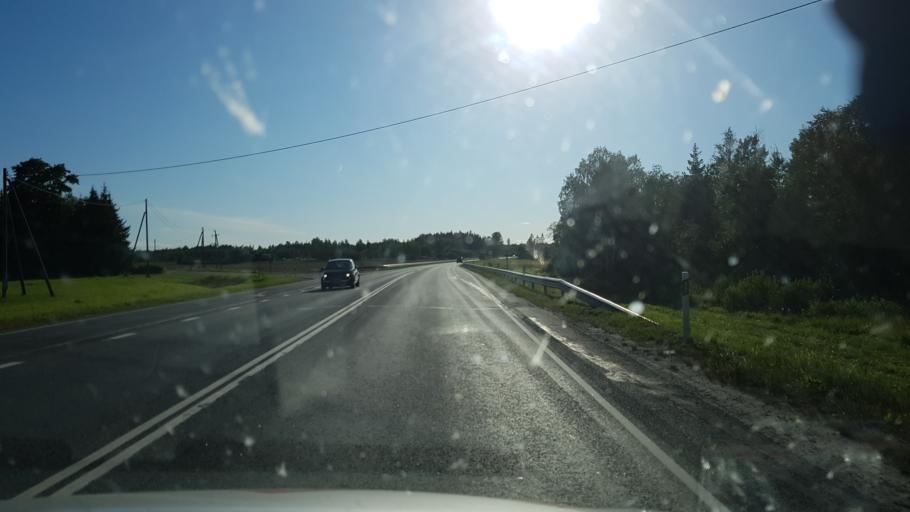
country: EE
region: Tartu
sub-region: Tartu linn
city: Tartu
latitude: 58.4097
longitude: 26.6278
